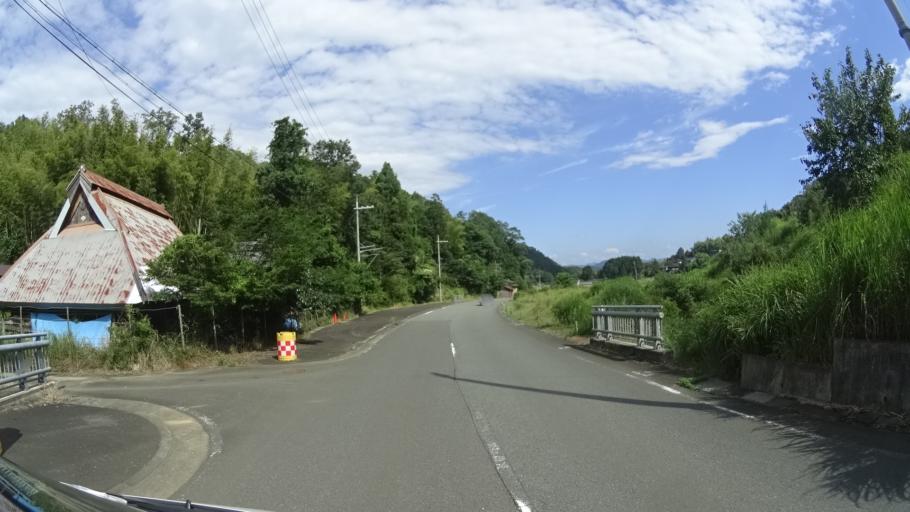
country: JP
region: Kyoto
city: Fukuchiyama
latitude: 35.3419
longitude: 135.1634
